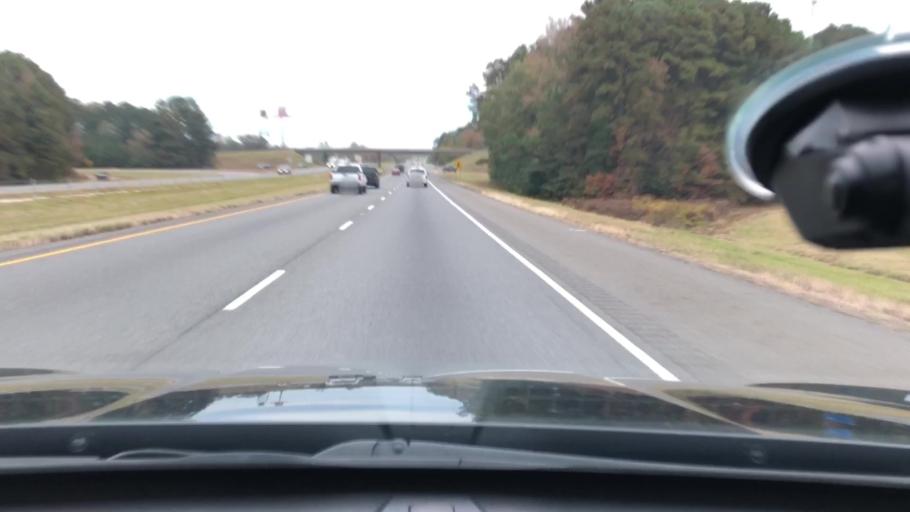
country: US
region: Arkansas
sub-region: Clark County
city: Gurdon
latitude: 33.9947
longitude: -93.1859
